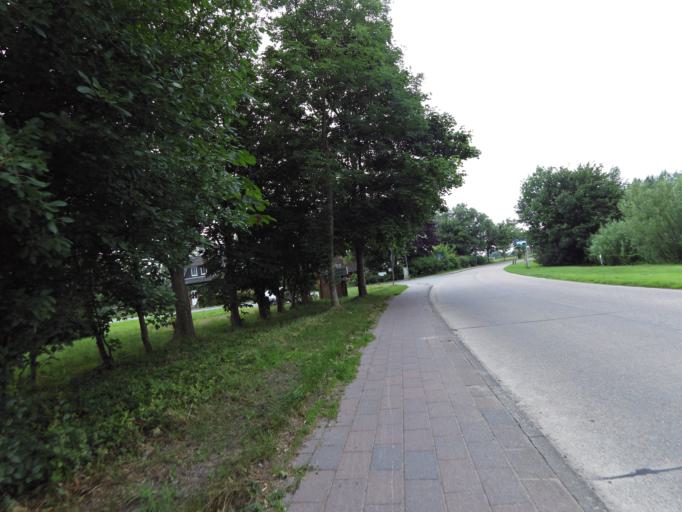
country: DE
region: Lower Saxony
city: Padingbuttel
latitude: 53.7277
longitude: 8.5322
